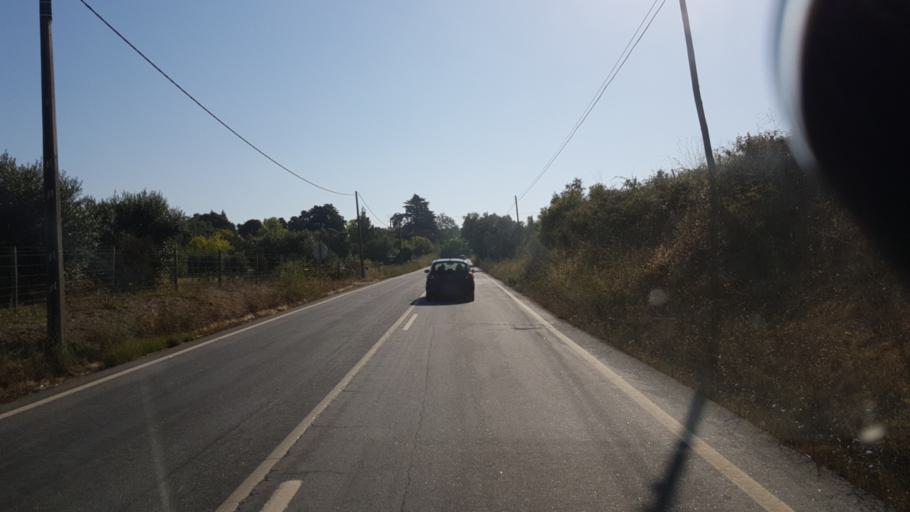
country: PT
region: Setubal
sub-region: Sesimbra
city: Sesimbra
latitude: 38.4977
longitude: -9.0511
